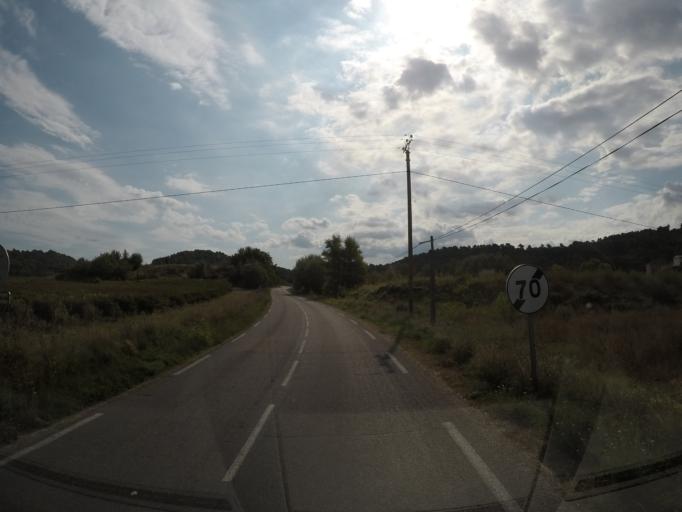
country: FR
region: Provence-Alpes-Cote d'Azur
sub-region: Departement du Vaucluse
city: Ansouis
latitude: 43.7343
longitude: 5.4852
